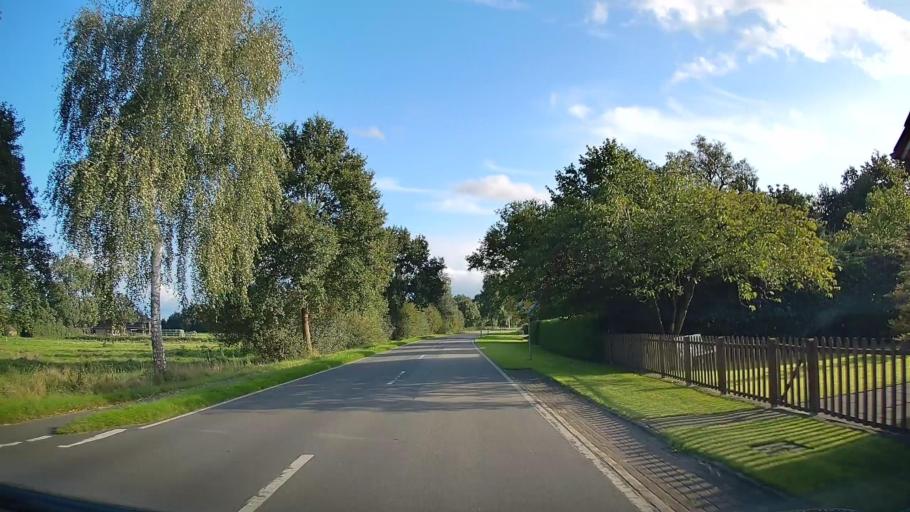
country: DE
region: Lower Saxony
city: Ostrhauderfehn
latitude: 53.1349
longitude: 7.6674
